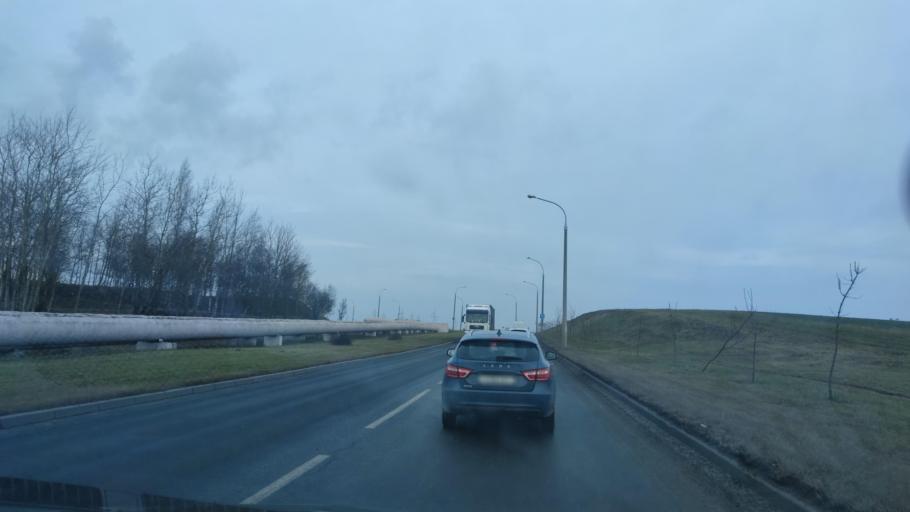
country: BY
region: Minsk
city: Malinovka
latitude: 53.8714
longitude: 27.4239
